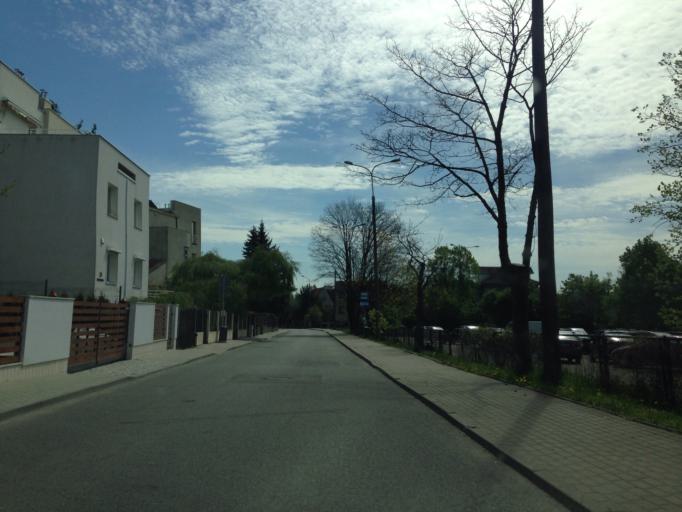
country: PL
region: Pomeranian Voivodeship
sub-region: Gdynia
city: Gdynia
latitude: 54.5129
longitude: 18.5466
